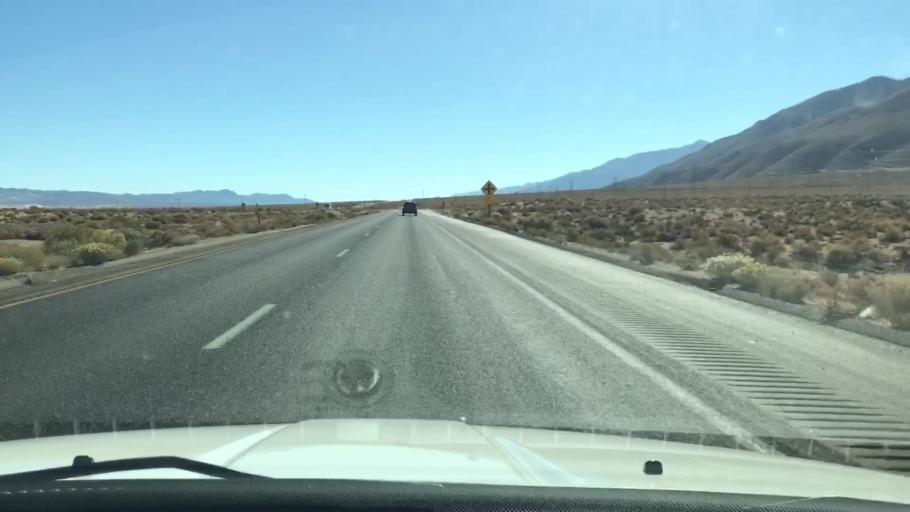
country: US
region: California
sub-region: Inyo County
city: Lone Pine
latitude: 36.4095
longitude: -118.0278
